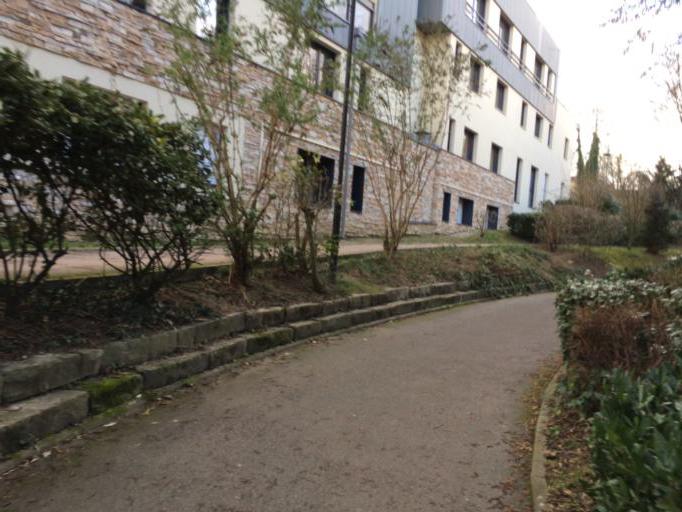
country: FR
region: Ile-de-France
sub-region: Departement des Hauts-de-Seine
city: Sceaux
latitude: 48.7821
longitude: 2.2873
